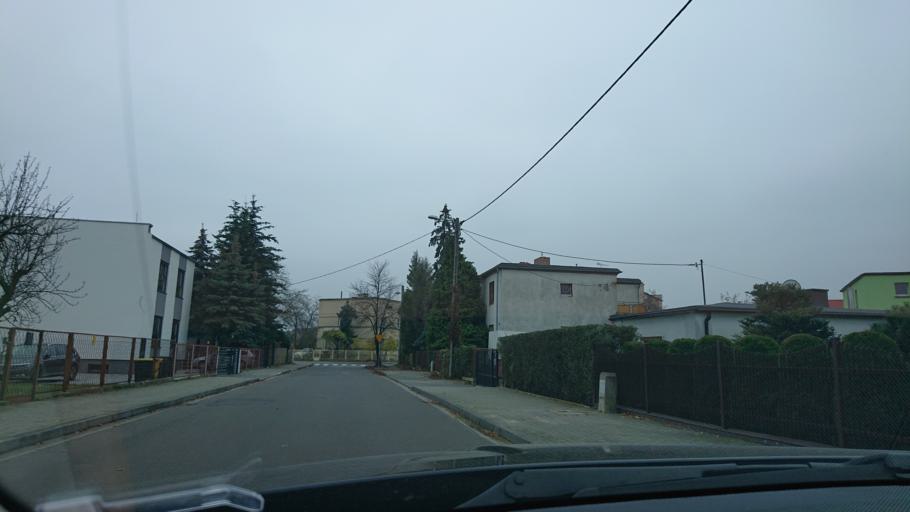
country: PL
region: Greater Poland Voivodeship
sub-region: Powiat gnieznienski
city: Gniezno
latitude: 52.5363
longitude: 17.6244
